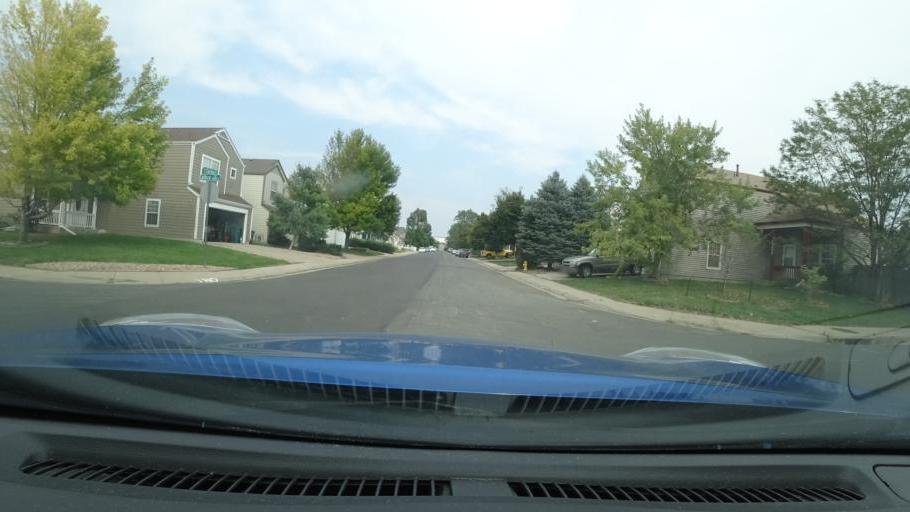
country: US
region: Colorado
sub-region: Adams County
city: Aurora
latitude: 39.7498
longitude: -104.7672
